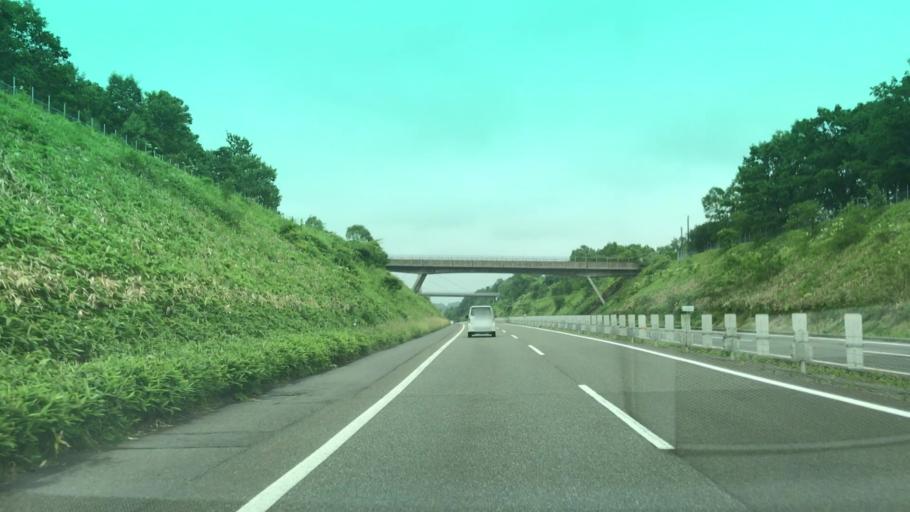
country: JP
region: Hokkaido
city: Tomakomai
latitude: 42.6205
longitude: 141.4769
